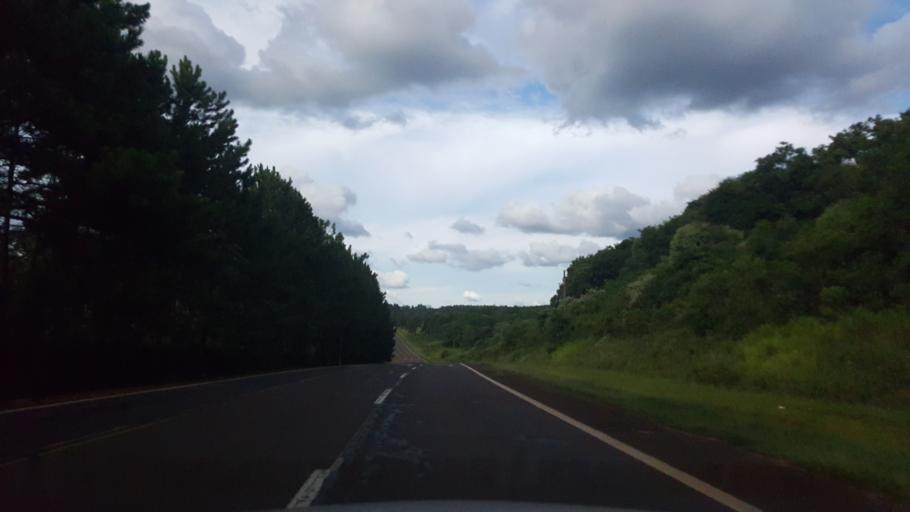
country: AR
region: Misiones
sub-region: Departamento de San Ignacio
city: San Ignacio
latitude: -27.2215
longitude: -55.5032
